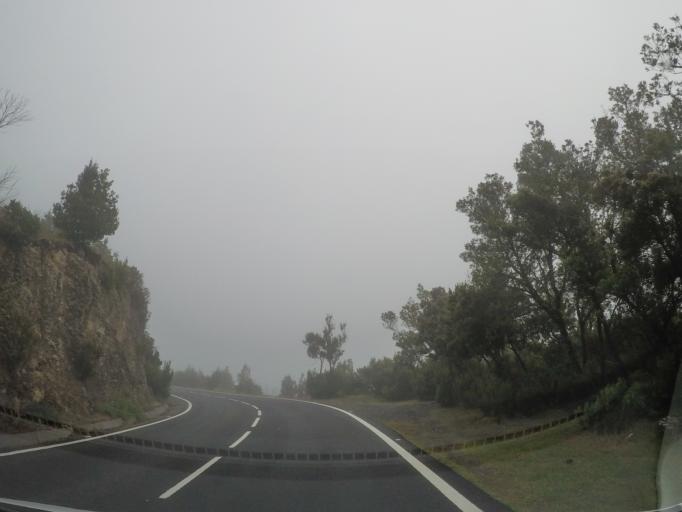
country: ES
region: Canary Islands
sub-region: Provincia de Santa Cruz de Tenerife
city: Vallehermosa
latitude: 28.1288
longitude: -17.2730
